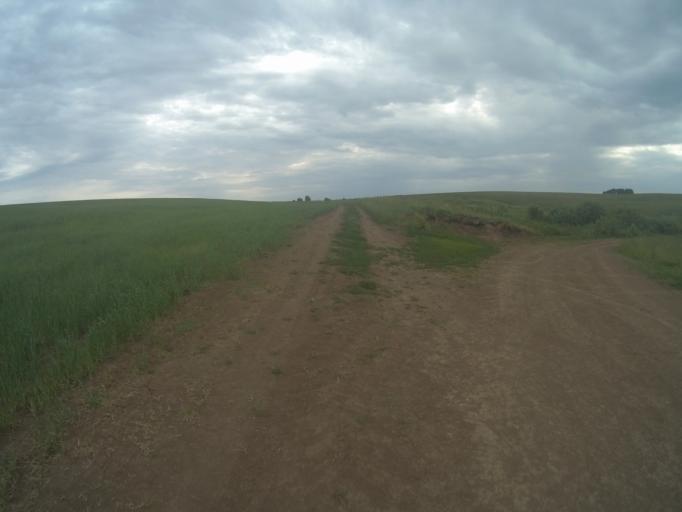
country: RU
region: Vladimir
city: Bogolyubovo
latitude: 56.2309
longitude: 40.4859
